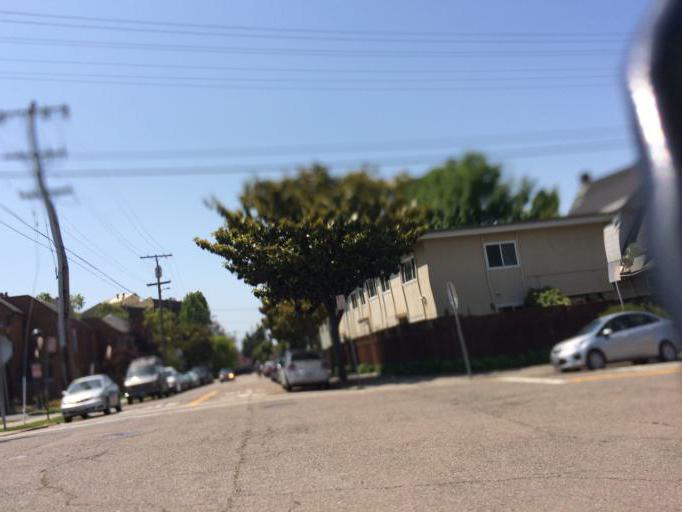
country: US
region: California
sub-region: Alameda County
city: Berkeley
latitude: 37.8583
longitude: -122.2693
